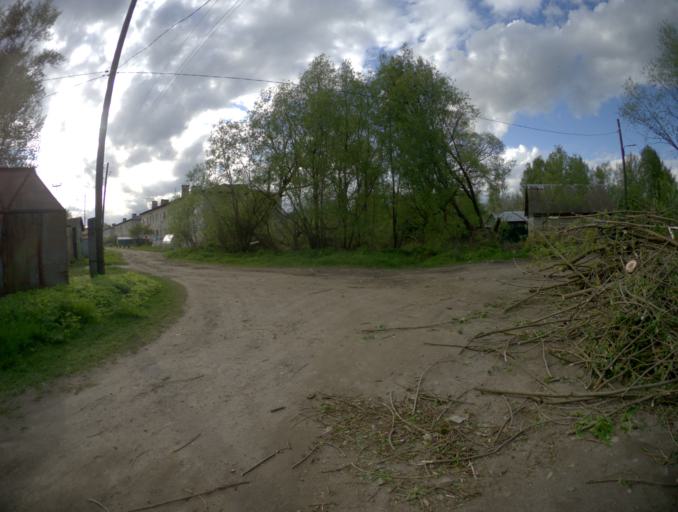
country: RU
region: Vladimir
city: Gusevskiy
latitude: 55.6589
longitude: 40.5585
